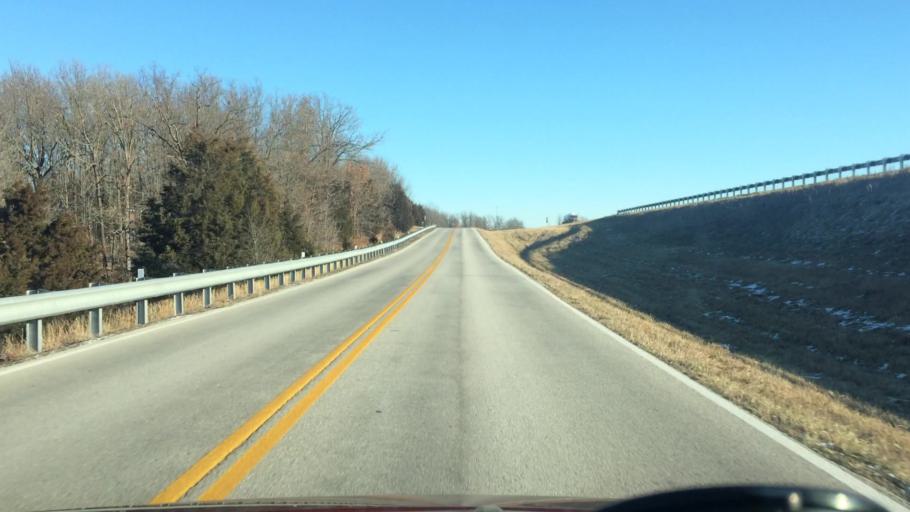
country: US
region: Missouri
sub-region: Greene County
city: Strafford
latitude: 37.2800
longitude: -93.0454
